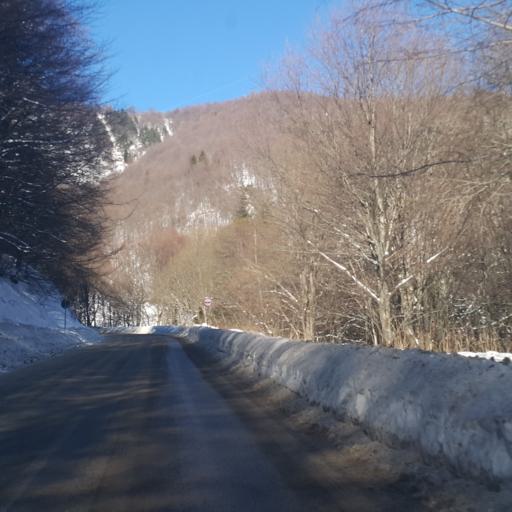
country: XK
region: Mitrovica
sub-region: Komuna e Leposaviqit
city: Leposaviq
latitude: 43.3082
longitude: 20.8581
